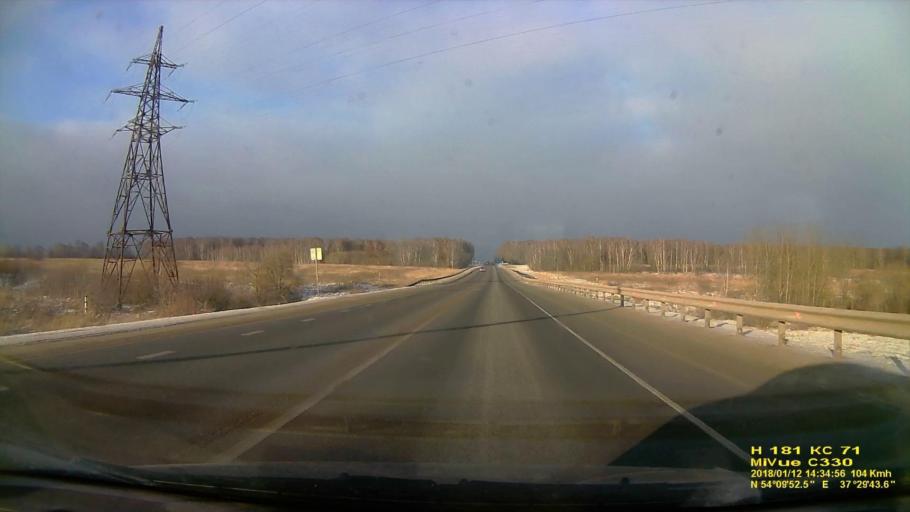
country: RU
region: Tula
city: Kosaya Gora
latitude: 54.1646
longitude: 37.4914
